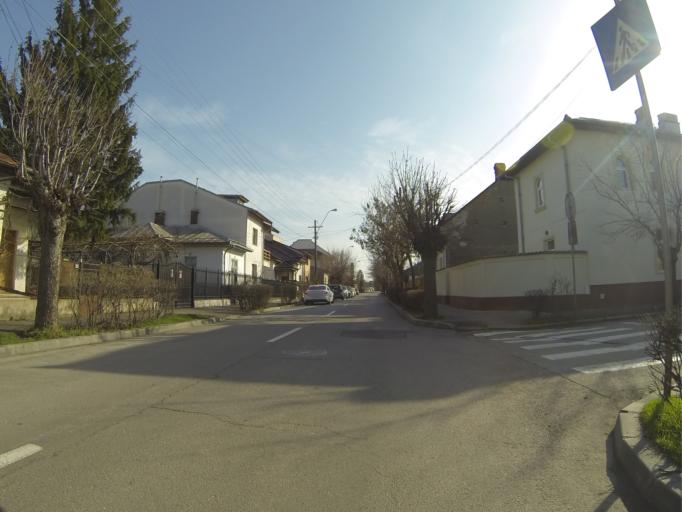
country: RO
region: Dolj
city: Craiova
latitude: 44.3150
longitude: 23.8150
